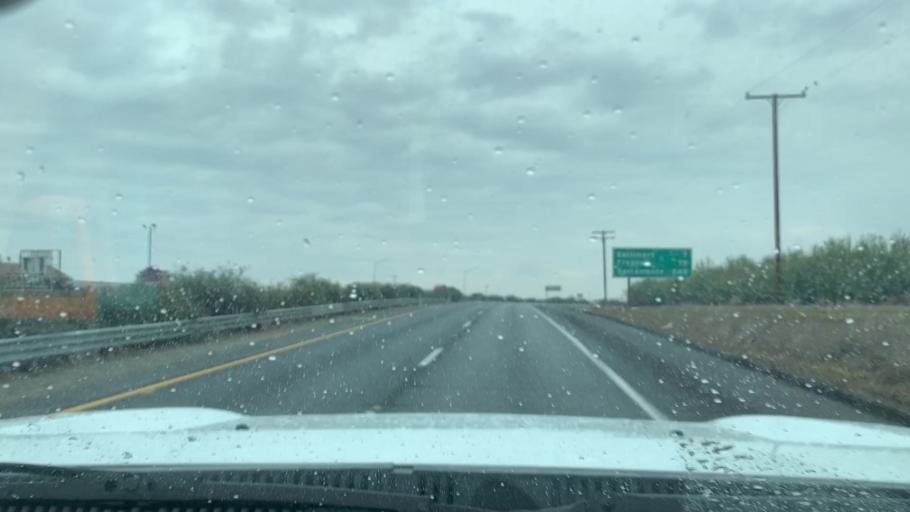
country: US
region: California
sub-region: Kern County
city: Delano
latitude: 35.7921
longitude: -119.2518
